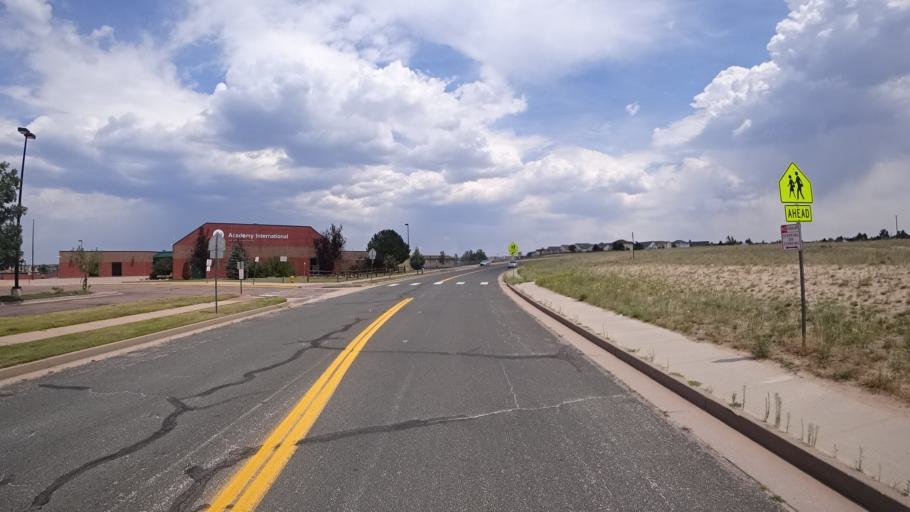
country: US
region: Colorado
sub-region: El Paso County
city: Black Forest
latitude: 38.9618
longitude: -104.7663
